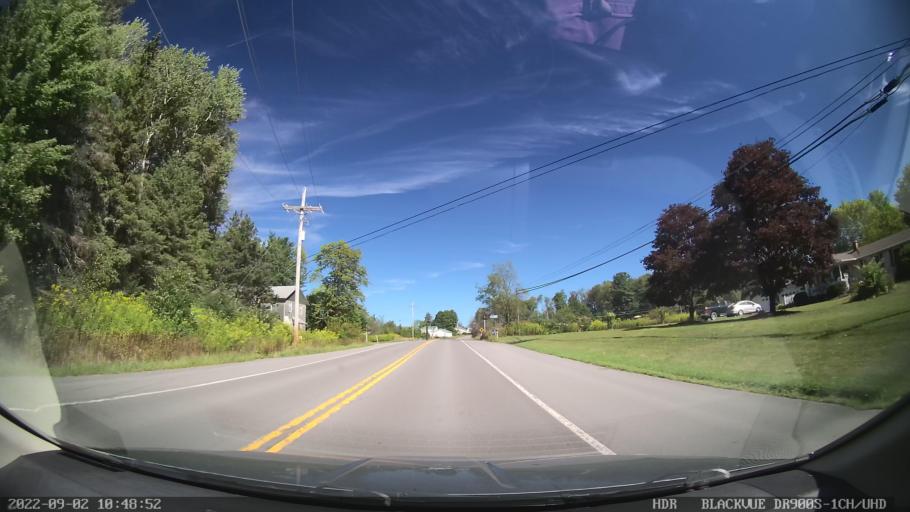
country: US
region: Pennsylvania
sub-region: Tioga County
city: Blossburg
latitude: 41.5927
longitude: -77.1097
